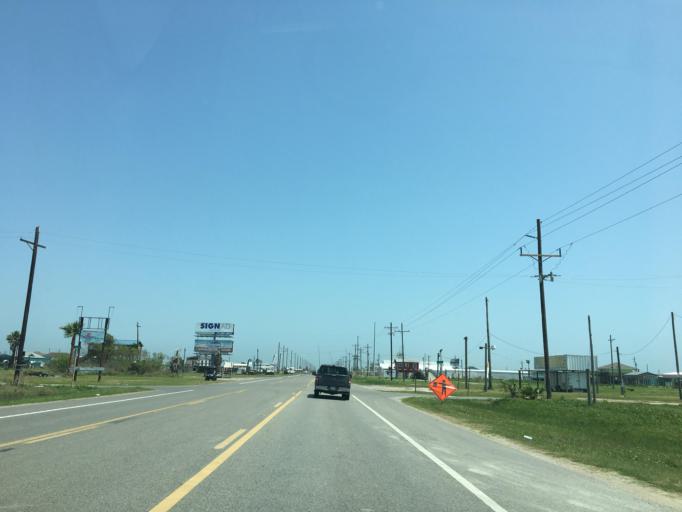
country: US
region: Texas
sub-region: Galveston County
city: Bolivar Peninsula
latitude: 29.4421
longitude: -94.6665
